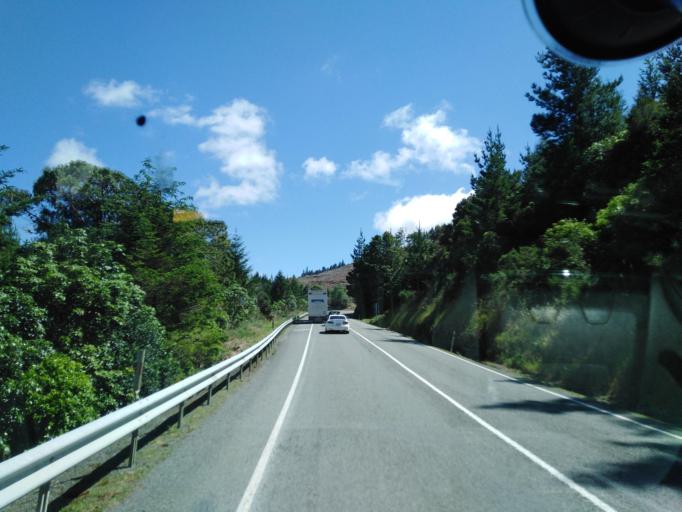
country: NZ
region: Nelson
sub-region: Nelson City
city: Nelson
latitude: -41.1963
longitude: 173.5583
